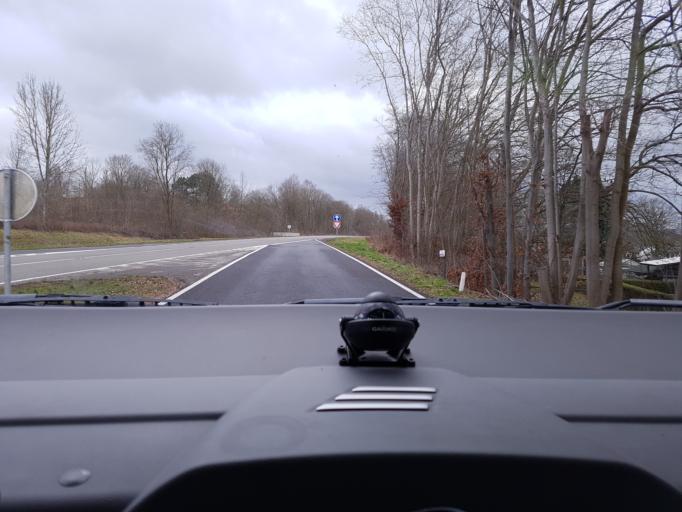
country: BE
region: Wallonia
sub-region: Province de Namur
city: Ciney
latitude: 50.2914
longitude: 5.1101
